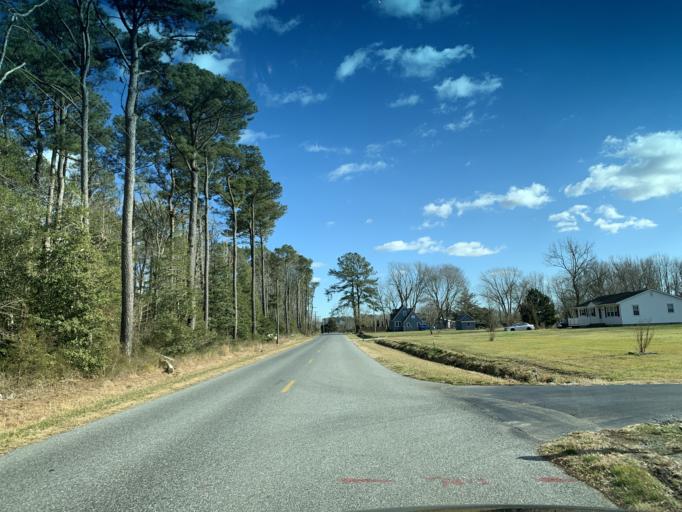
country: US
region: Maryland
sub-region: Worcester County
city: Berlin
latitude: 38.3671
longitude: -75.2046
